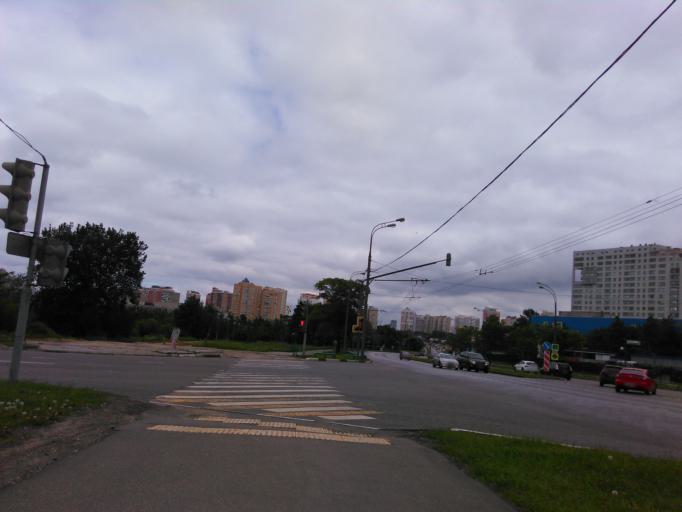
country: RU
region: Moscow
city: Troparevo
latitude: 55.6660
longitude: 37.4847
